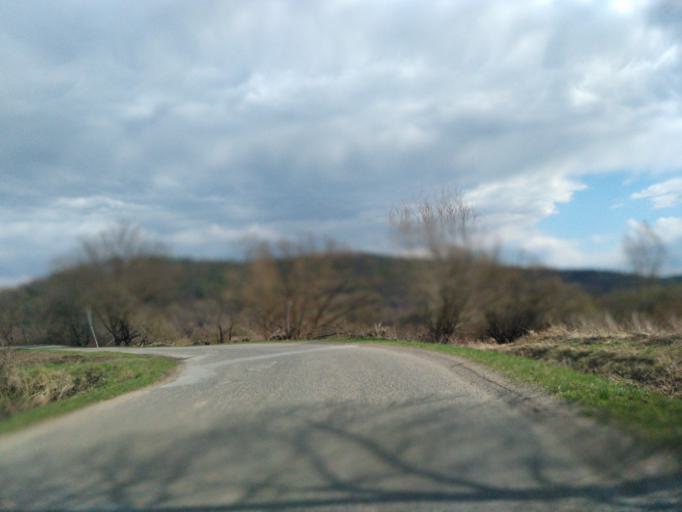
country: PL
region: Subcarpathian Voivodeship
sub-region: Powiat sanocki
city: Tyrawa Woloska
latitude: 49.6358
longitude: 22.2843
